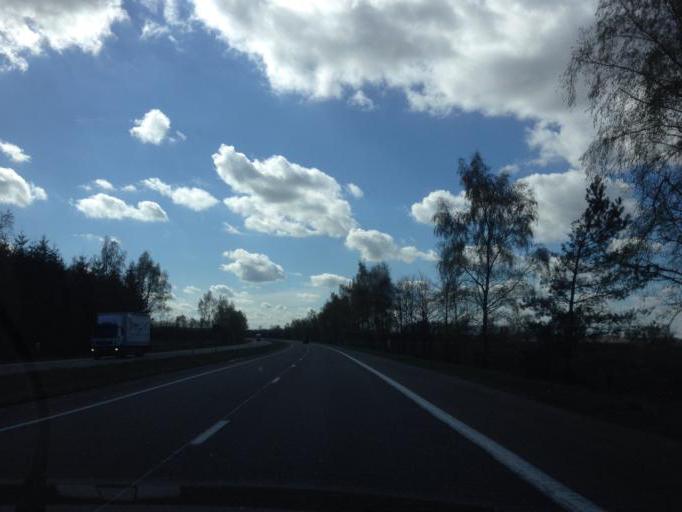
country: BE
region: Flanders
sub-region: Provincie Limburg
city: Overpelt
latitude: 51.2594
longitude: 5.3975
